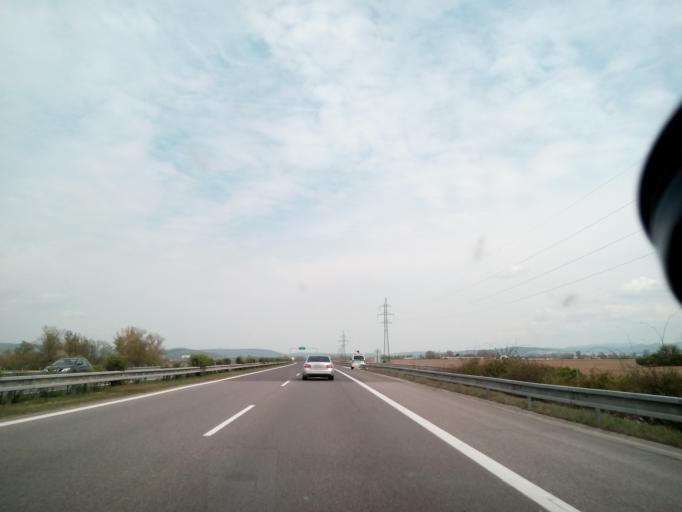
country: SK
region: Trenciansky
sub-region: Okres Trencin
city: Trencin
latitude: 48.8378
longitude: 17.9363
